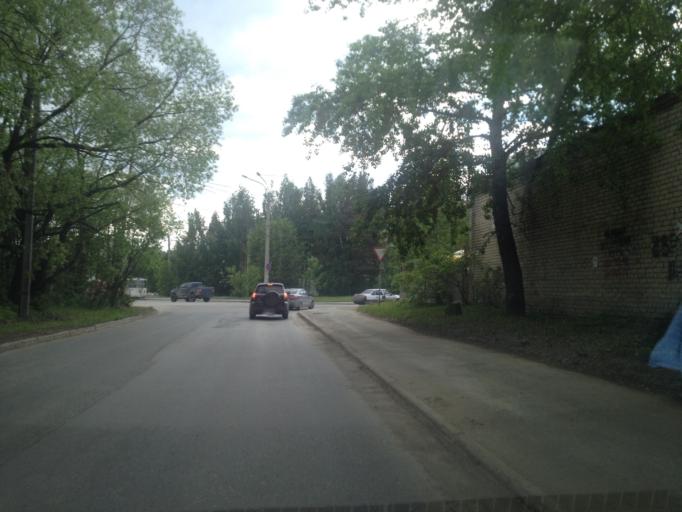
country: RU
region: Sverdlovsk
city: Sovkhoznyy
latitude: 56.7671
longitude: 60.5508
